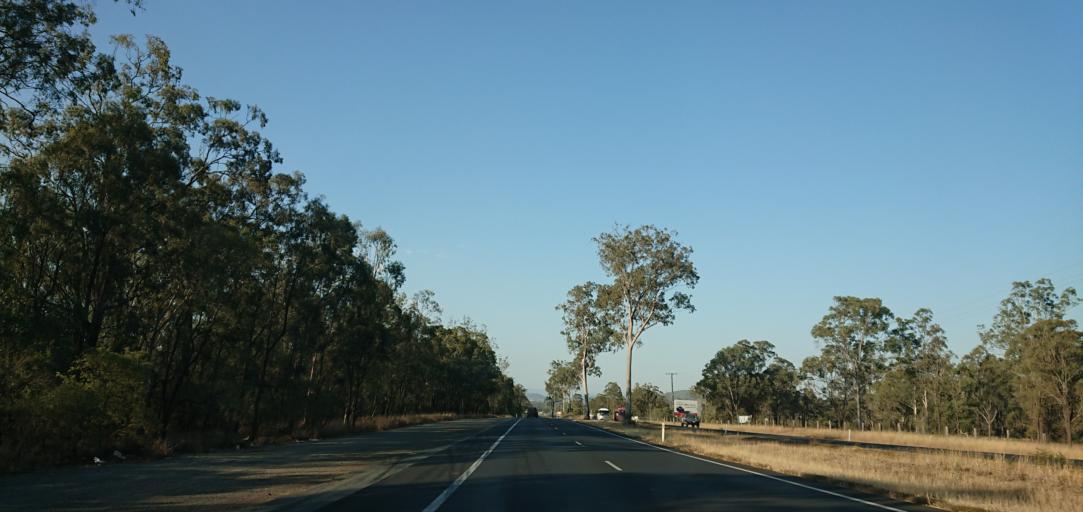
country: AU
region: Queensland
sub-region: Ipswich
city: Thagoona
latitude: -27.5607
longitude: 152.4746
